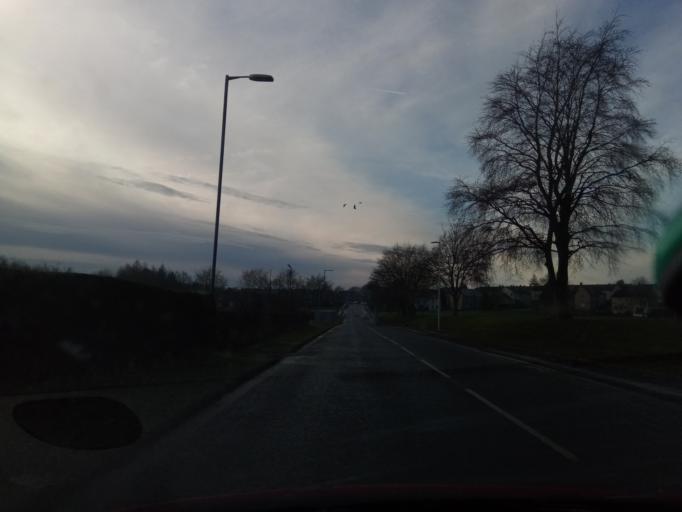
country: GB
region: Scotland
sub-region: The Scottish Borders
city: Hawick
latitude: 55.4378
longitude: -2.7617
